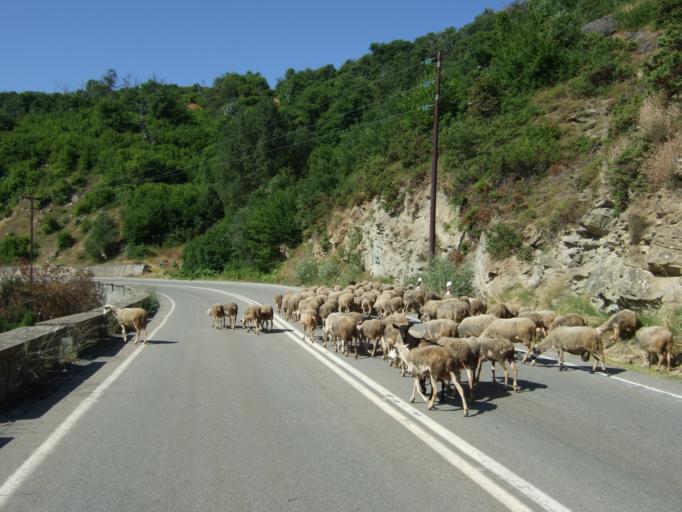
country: GR
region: West Macedonia
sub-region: Nomos Kozanis
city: Tsotili
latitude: 40.2013
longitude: 21.1525
